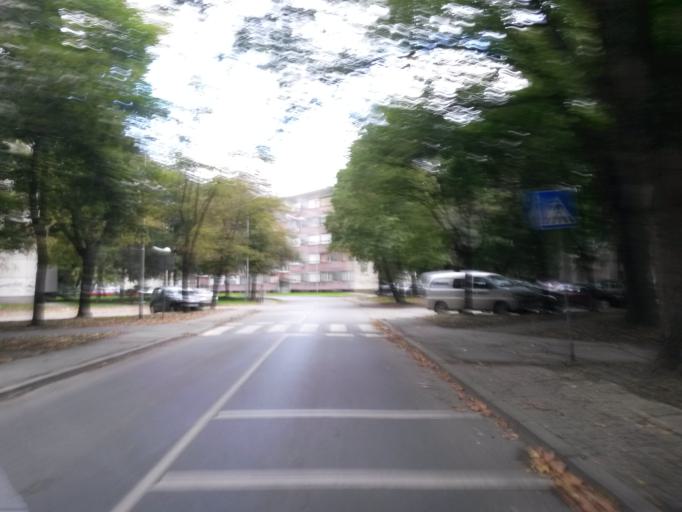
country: HR
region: Osjecko-Baranjska
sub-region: Grad Osijek
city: Osijek
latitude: 45.5531
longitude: 18.7003
